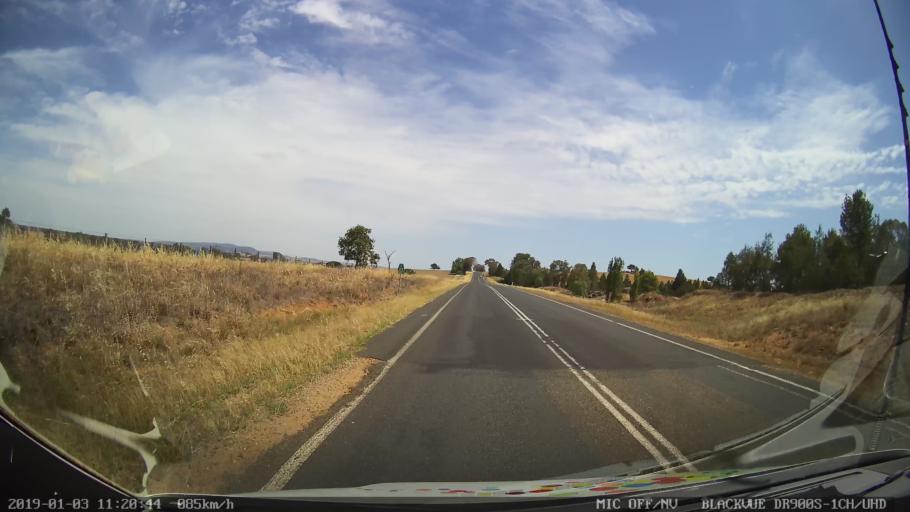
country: AU
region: New South Wales
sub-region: Weddin
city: Grenfell
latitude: -34.0973
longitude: 148.2538
